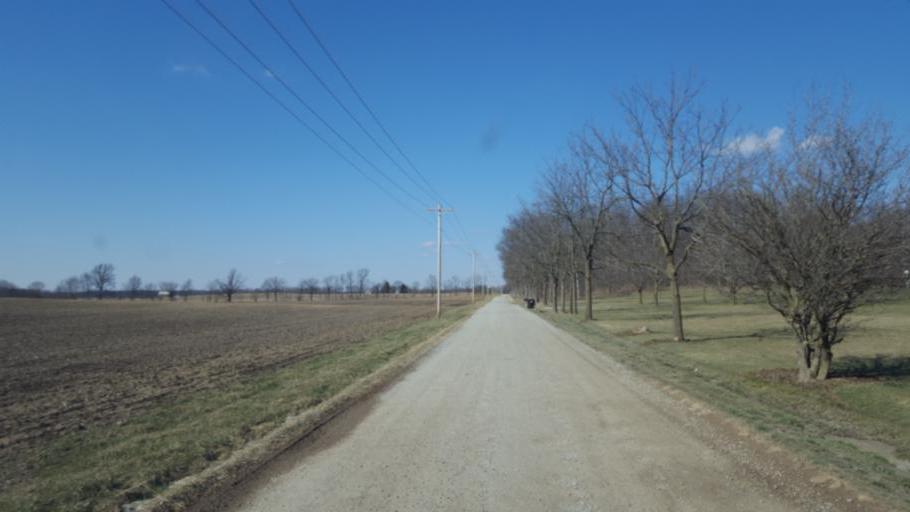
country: US
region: Ohio
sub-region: Morrow County
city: Mount Gilead
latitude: 40.4980
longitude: -82.7721
